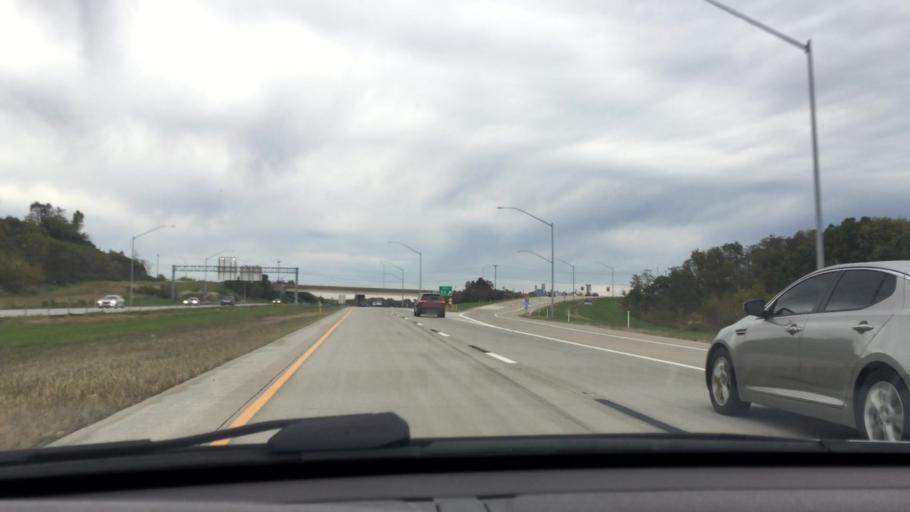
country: US
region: Pennsylvania
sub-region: Allegheny County
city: Imperial
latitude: 40.4960
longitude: -80.2781
